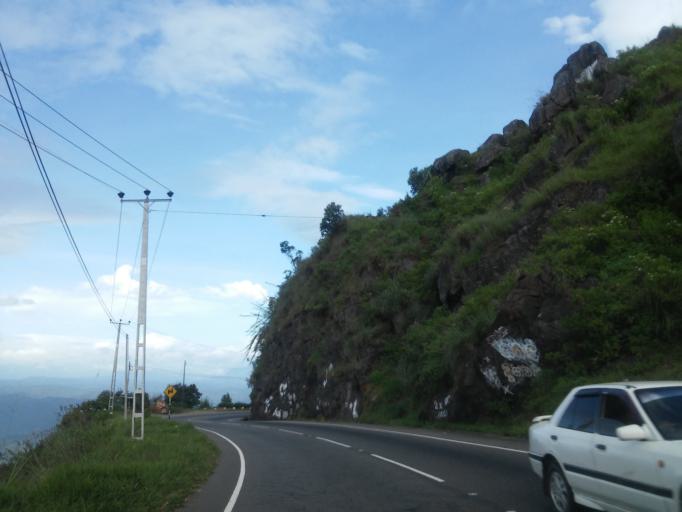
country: LK
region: Uva
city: Haputale
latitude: 6.7590
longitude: 80.9460
